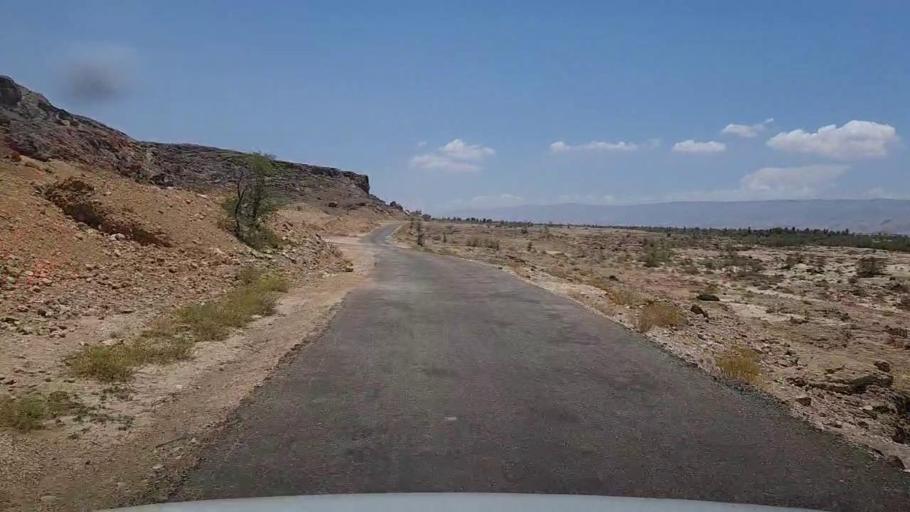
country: PK
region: Sindh
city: Bhan
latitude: 26.2903
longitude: 67.5329
